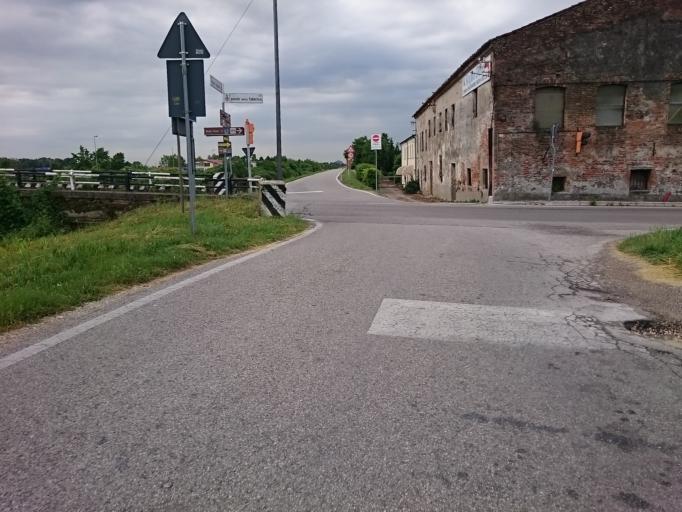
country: IT
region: Veneto
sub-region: Provincia di Padova
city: Mandriola-Sant'Agostino
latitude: 45.3534
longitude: 11.8341
